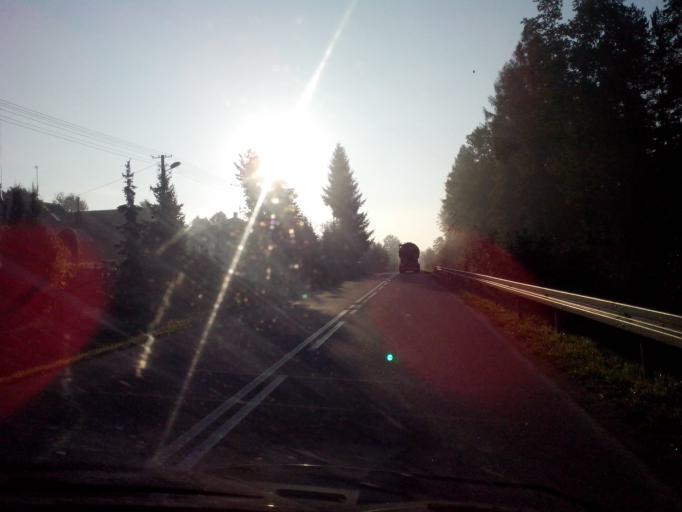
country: PL
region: Subcarpathian Voivodeship
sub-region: Powiat brzozowski
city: Wesola
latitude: 49.8377
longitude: 22.1398
